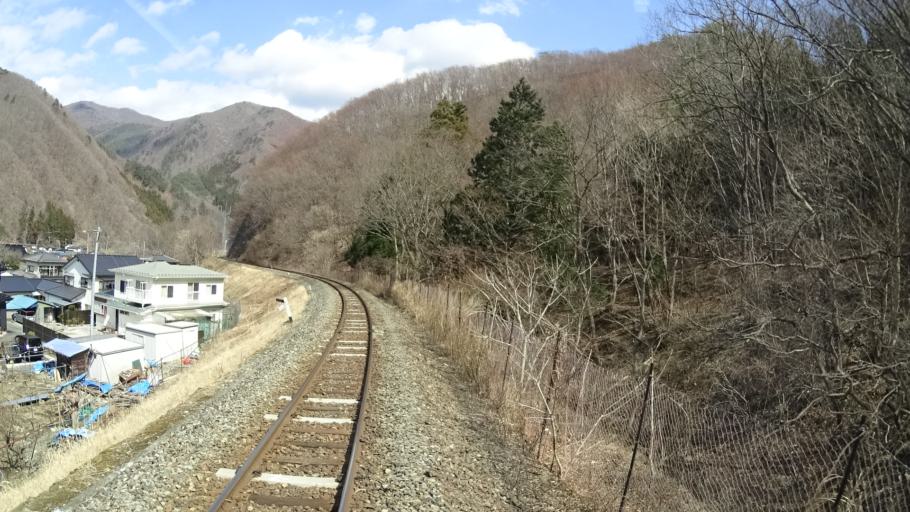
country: JP
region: Iwate
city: Kamaishi
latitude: 39.2518
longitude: 141.7421
